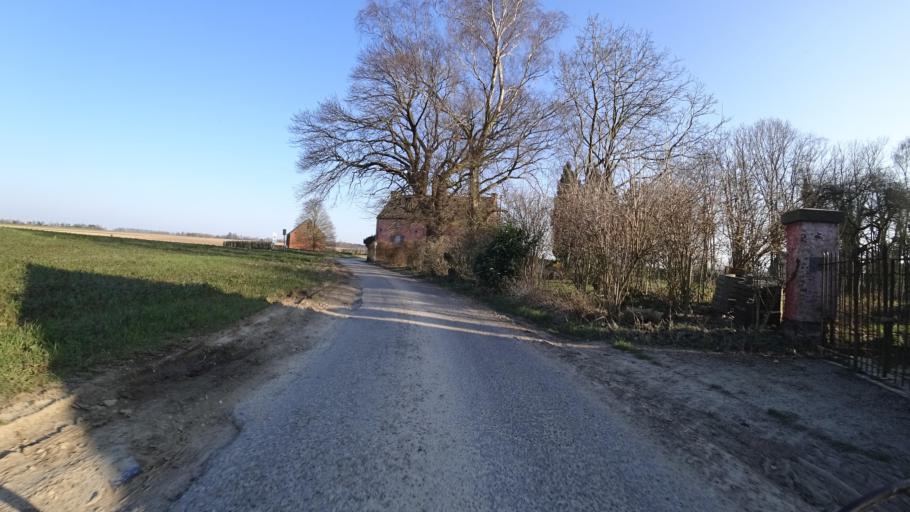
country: BE
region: Wallonia
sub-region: Province du Brabant Wallon
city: Chastre
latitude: 50.5833
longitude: 4.6490
